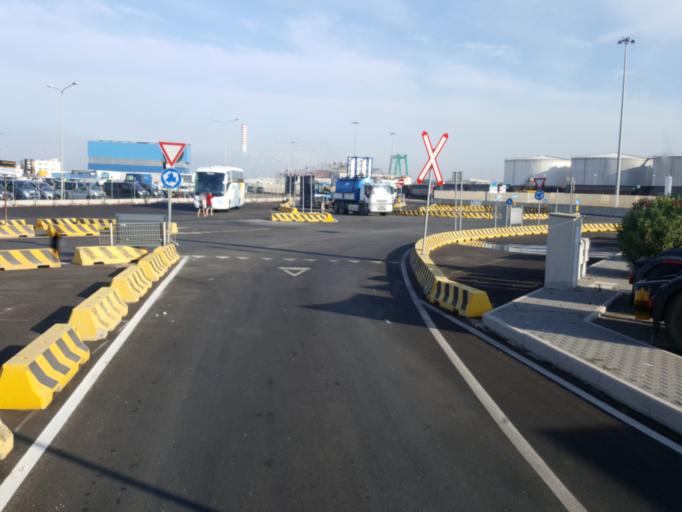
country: IT
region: Latium
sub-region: Citta metropolitana di Roma Capitale
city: Civitavecchia
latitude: 42.1051
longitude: 11.7787
